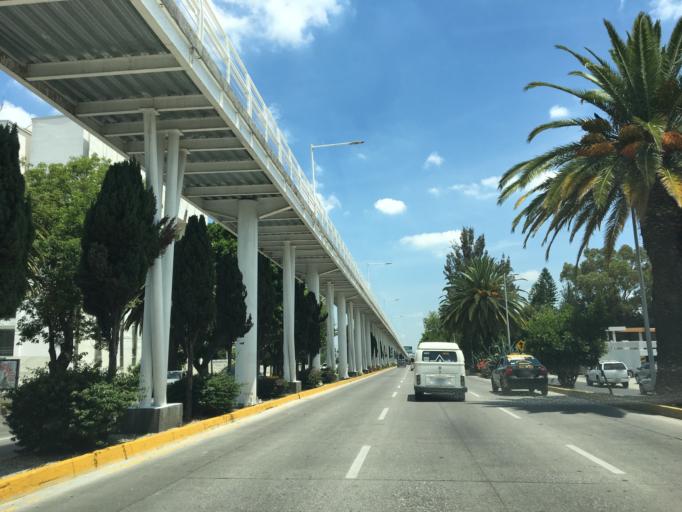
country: MX
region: Puebla
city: Puebla
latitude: 19.0670
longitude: -98.2240
